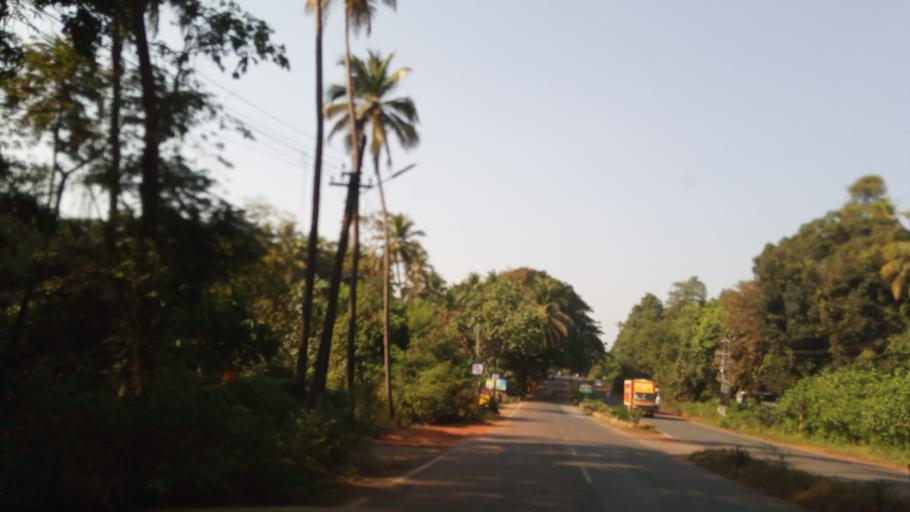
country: IN
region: Goa
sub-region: North Goa
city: Bandora
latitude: 15.4666
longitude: 73.9624
